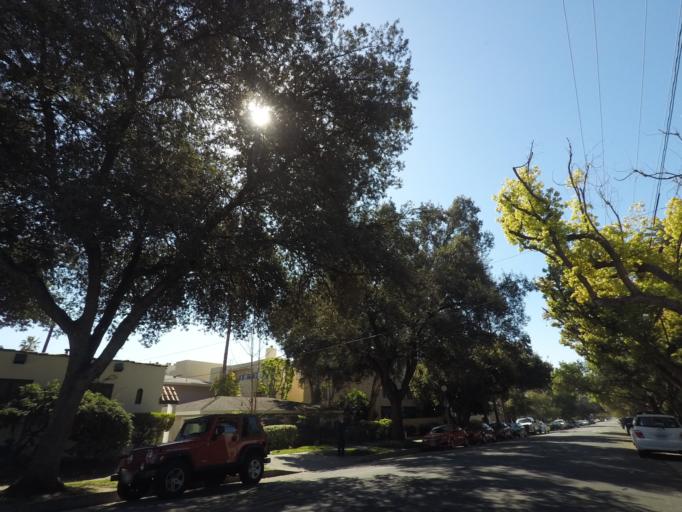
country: US
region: California
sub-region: Los Angeles County
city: Pasadena
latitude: 34.1380
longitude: -118.1429
